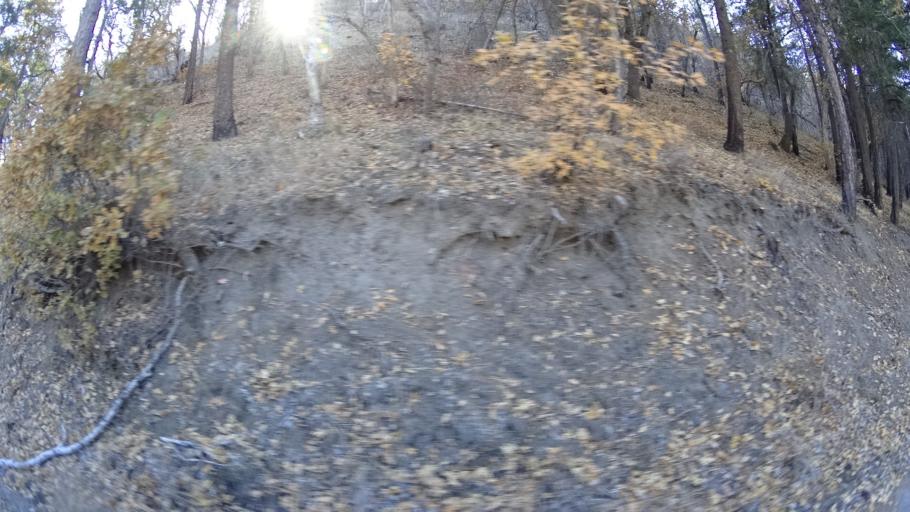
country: US
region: California
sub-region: Siskiyou County
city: Yreka
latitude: 41.8466
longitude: -122.6864
